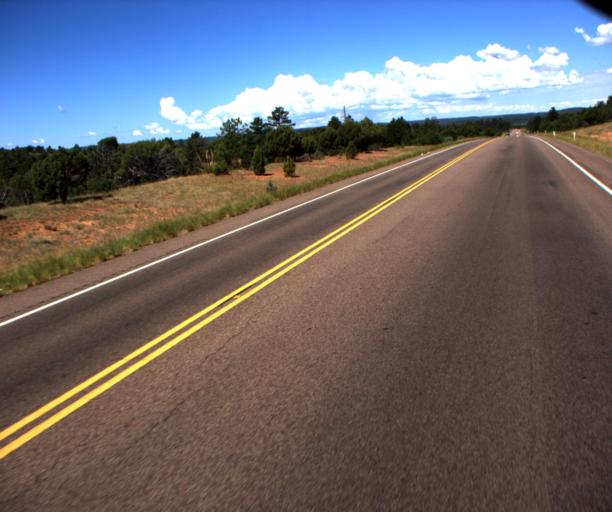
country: US
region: Arizona
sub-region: Navajo County
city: Linden
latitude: 34.2964
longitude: -110.1893
